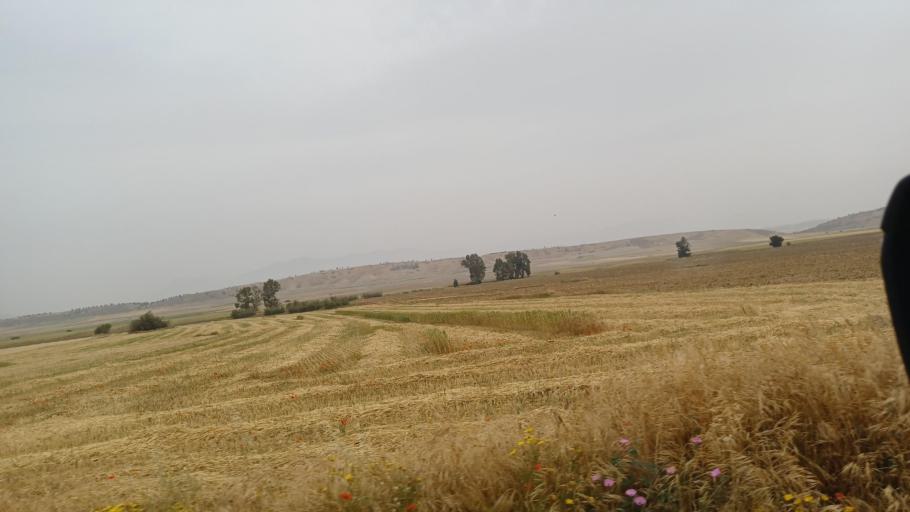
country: CY
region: Lefkosia
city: Mammari
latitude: 35.1853
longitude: 33.1775
